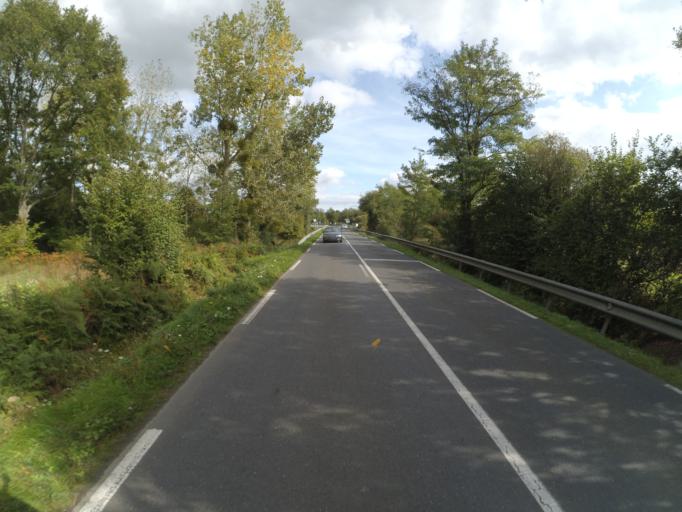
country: FR
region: Pays de la Loire
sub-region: Departement de la Loire-Atlantique
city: Notre-Dame-des-Landes
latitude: 47.4076
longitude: -1.7339
